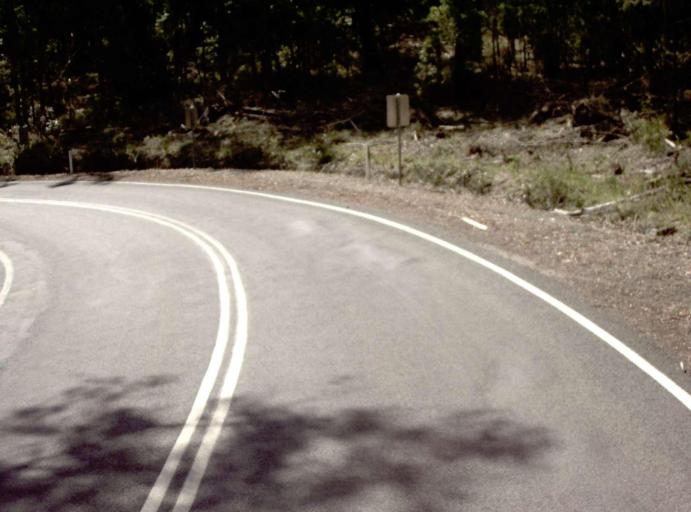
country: AU
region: New South Wales
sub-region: Bega Valley
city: Eden
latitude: -37.5323
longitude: 149.6945
